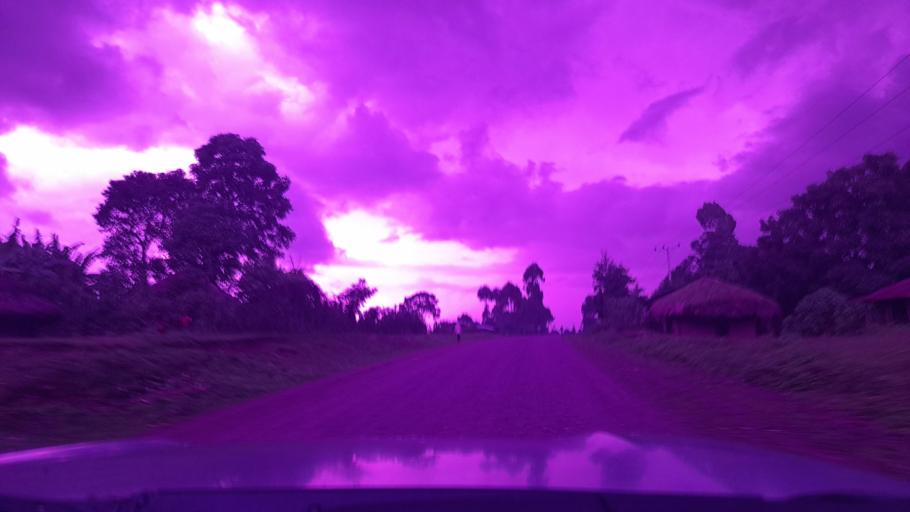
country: ET
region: Southern Nations, Nationalities, and People's Region
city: Mizan Teferi
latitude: 6.8987
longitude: 35.8423
